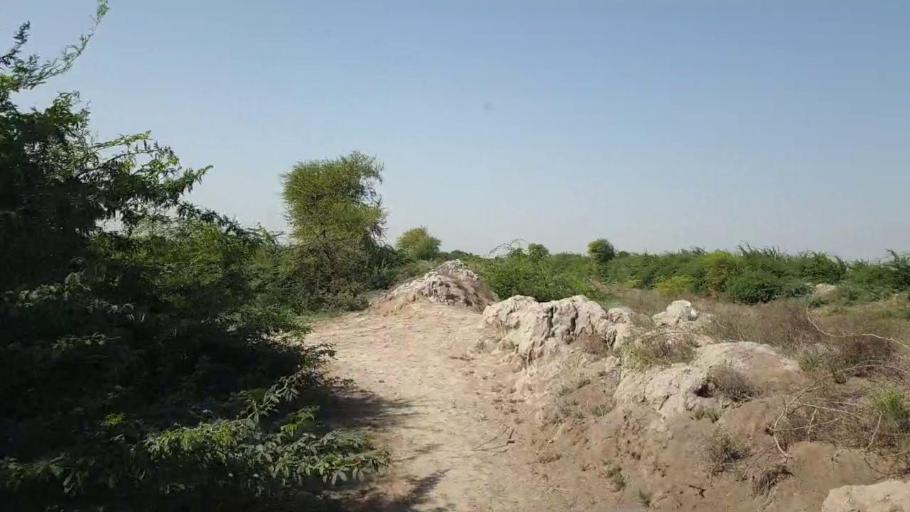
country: PK
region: Sindh
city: Tando Bago
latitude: 24.7456
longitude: 69.0267
